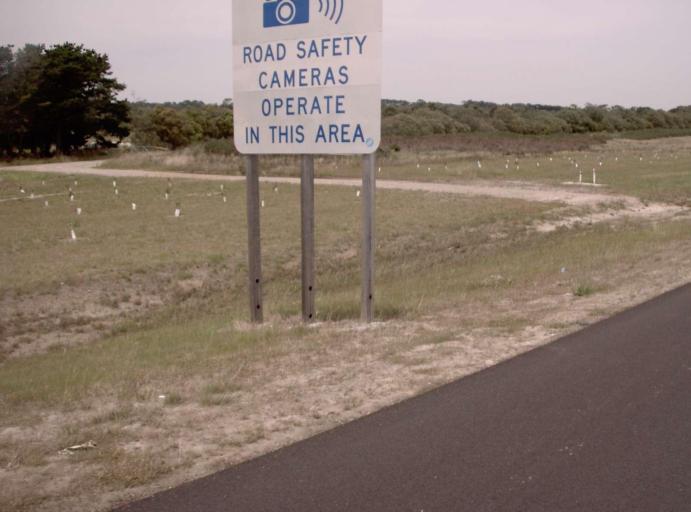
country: AU
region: Victoria
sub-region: Mornington Peninsula
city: Moorooduc
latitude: -38.2428
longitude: 145.1225
